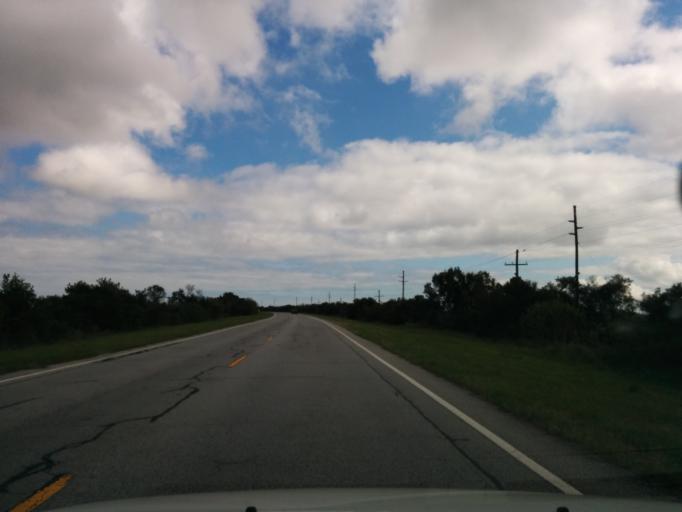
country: US
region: Georgia
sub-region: Glynn County
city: Brunswick
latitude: 31.0786
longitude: -81.4716
